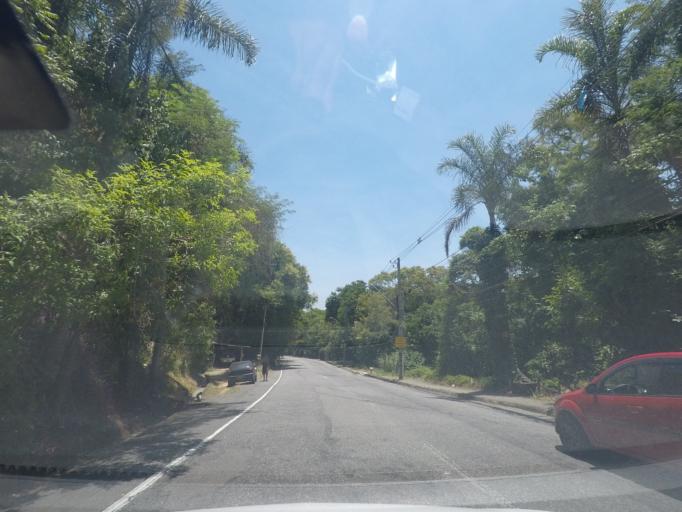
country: BR
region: Rio de Janeiro
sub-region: Niteroi
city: Niteroi
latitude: -22.9211
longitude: -43.0656
